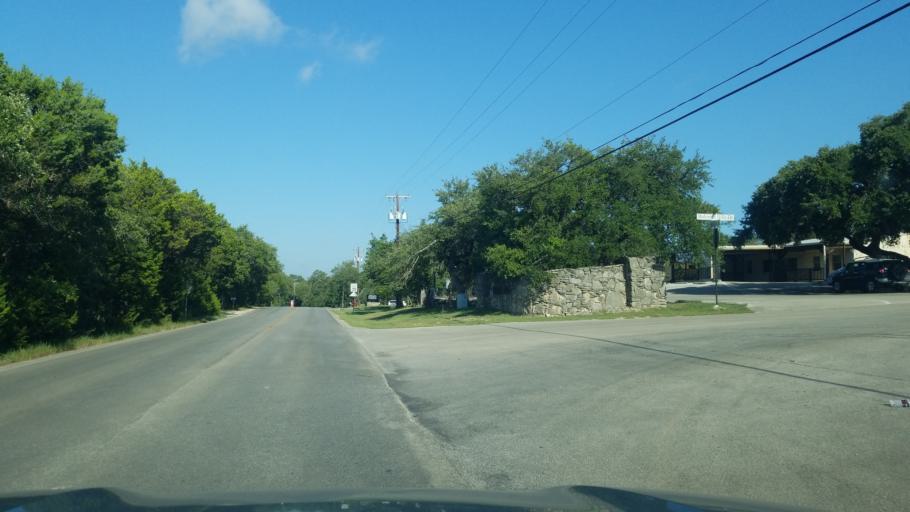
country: US
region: Texas
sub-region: Comal County
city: Bulverde
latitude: 29.7424
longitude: -98.4426
